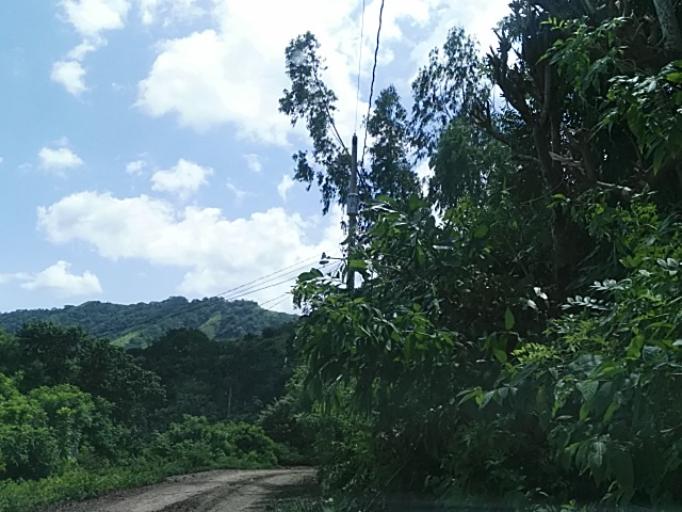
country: NI
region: Matagalpa
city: Terrabona
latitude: 12.7387
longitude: -85.9251
